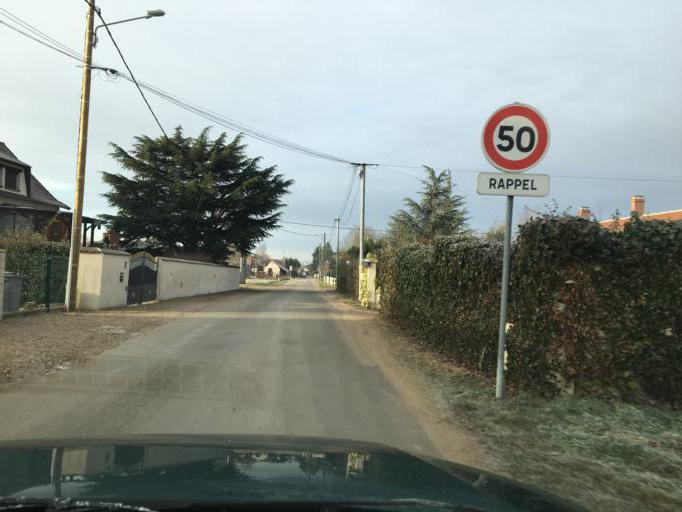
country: FR
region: Centre
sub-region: Departement du Loiret
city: Clery-Saint-Andre
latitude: 47.8126
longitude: 1.7440
